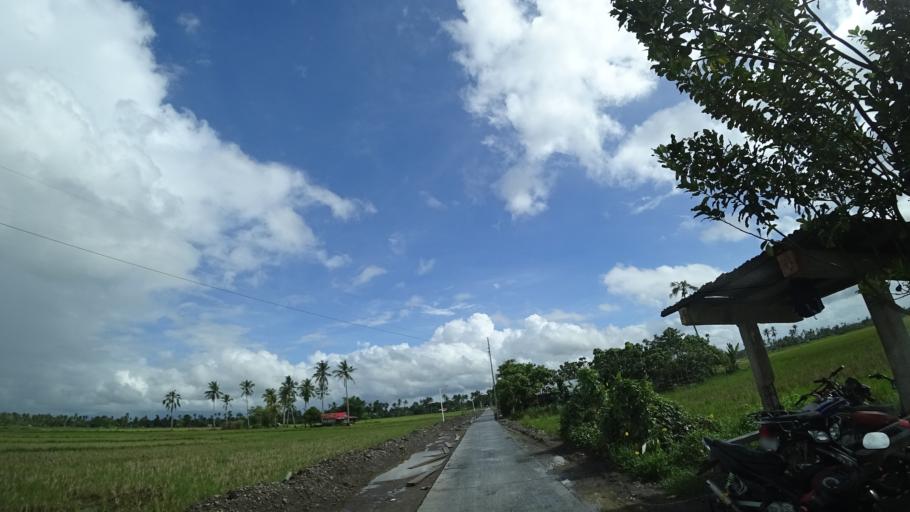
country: PH
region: Eastern Visayas
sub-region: Province of Leyte
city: Cabacungan
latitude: 10.9108
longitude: 124.9775
